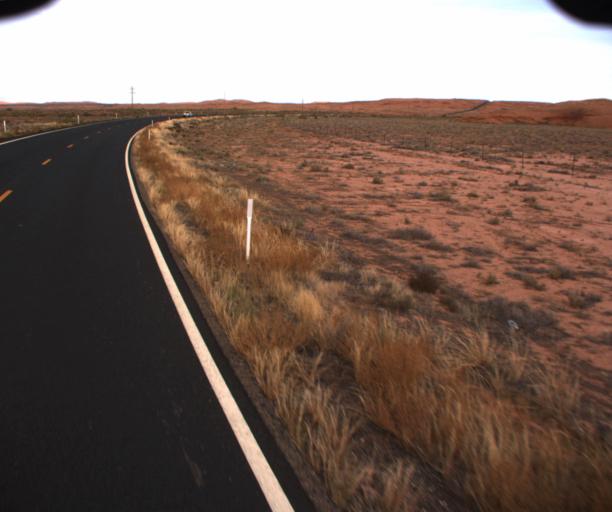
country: US
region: Arizona
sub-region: Apache County
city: Many Farms
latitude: 36.7725
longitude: -109.6612
